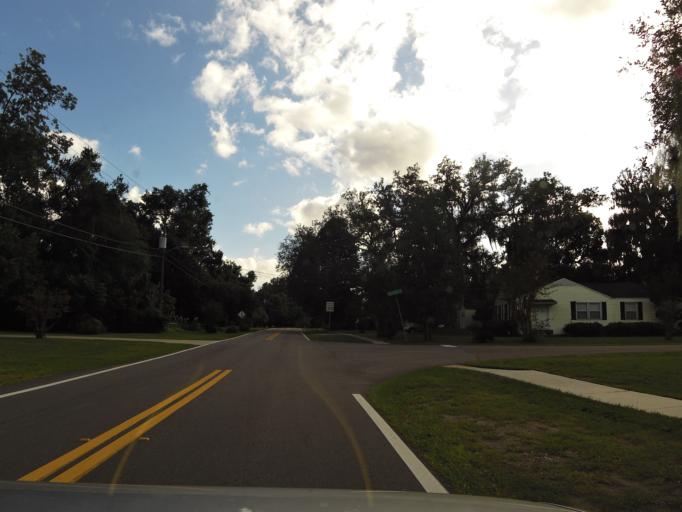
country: US
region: Florida
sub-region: Duval County
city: Jacksonville
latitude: 30.2704
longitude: -81.7238
